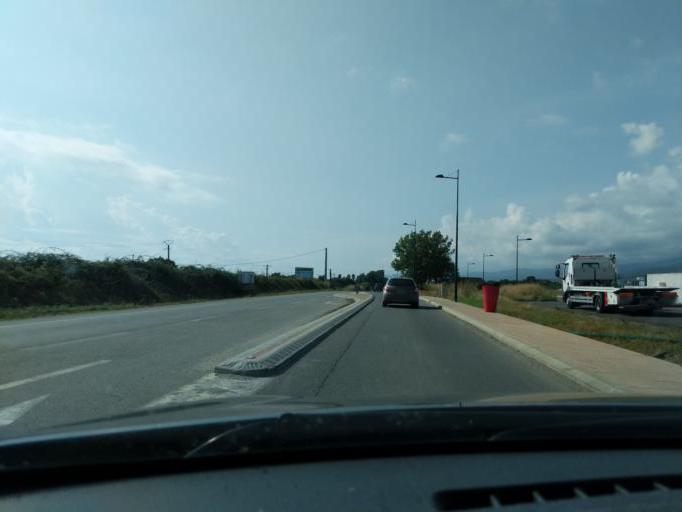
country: FR
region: Corsica
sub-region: Departement de la Haute-Corse
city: Ghisonaccia
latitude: 41.9929
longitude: 9.4021
